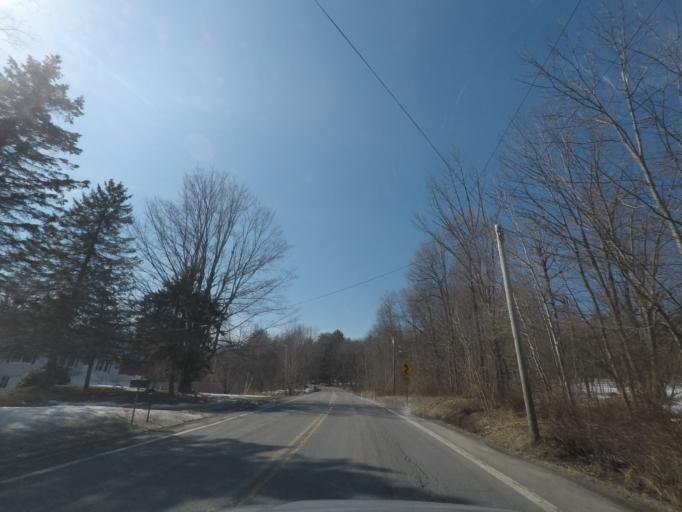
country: US
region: Massachusetts
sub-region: Berkshire County
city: Lanesborough
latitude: 42.5529
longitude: -73.3907
